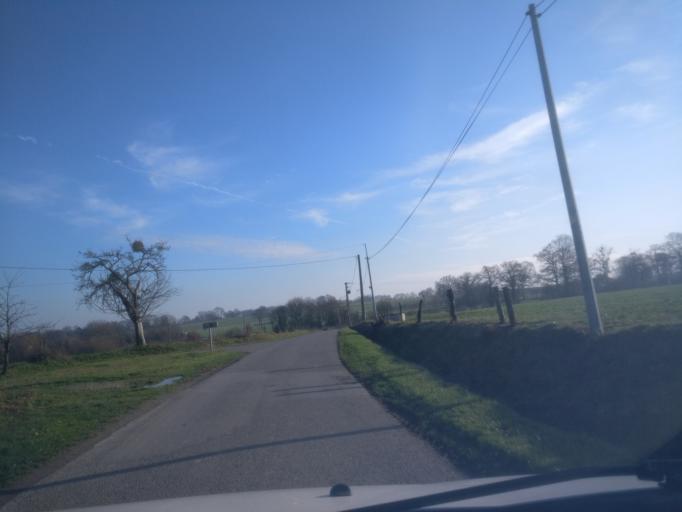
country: FR
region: Brittany
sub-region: Departement d'Ille-et-Vilaine
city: Livre-sur-Changeon
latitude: 48.2155
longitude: -1.3088
